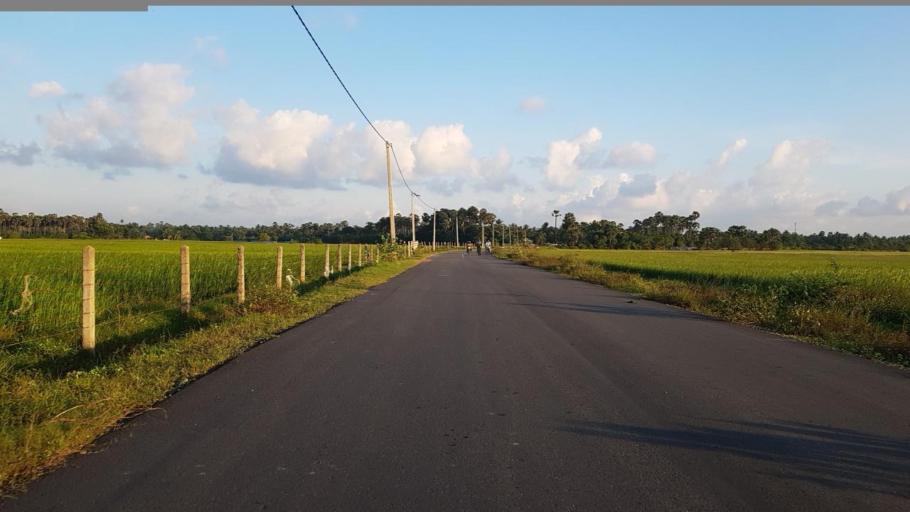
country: LK
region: Northern Province
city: Jaffna
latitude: 9.7255
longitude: 79.9754
